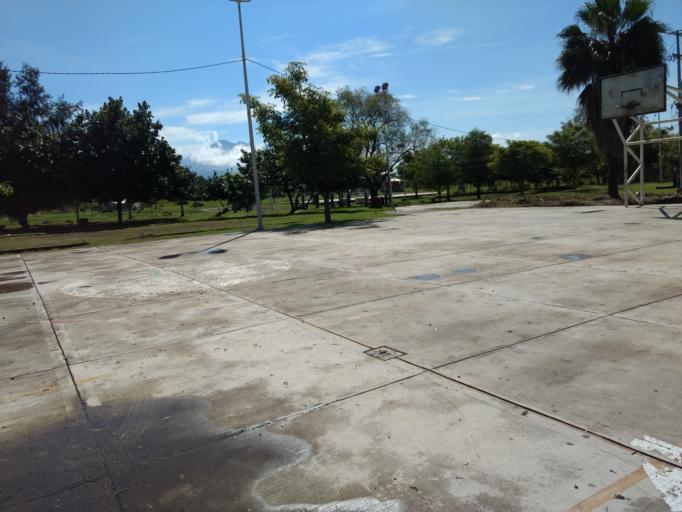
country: MX
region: Nayarit
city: Tepic
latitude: 21.4889
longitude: -104.8603
